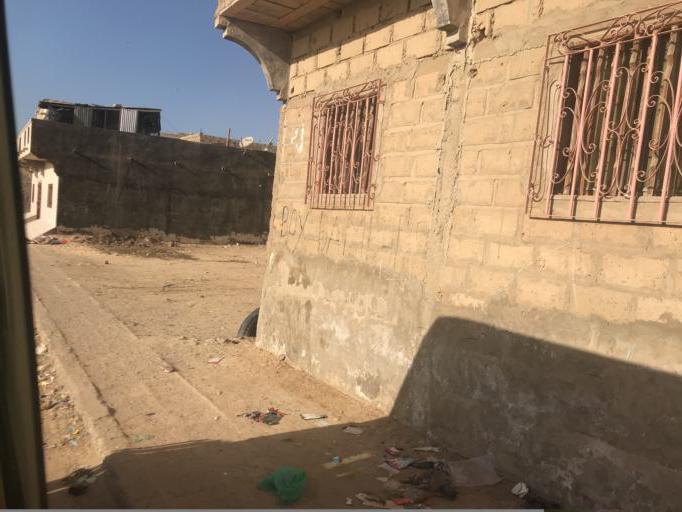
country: SN
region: Saint-Louis
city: Saint-Louis
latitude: 15.9964
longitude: -16.4938
